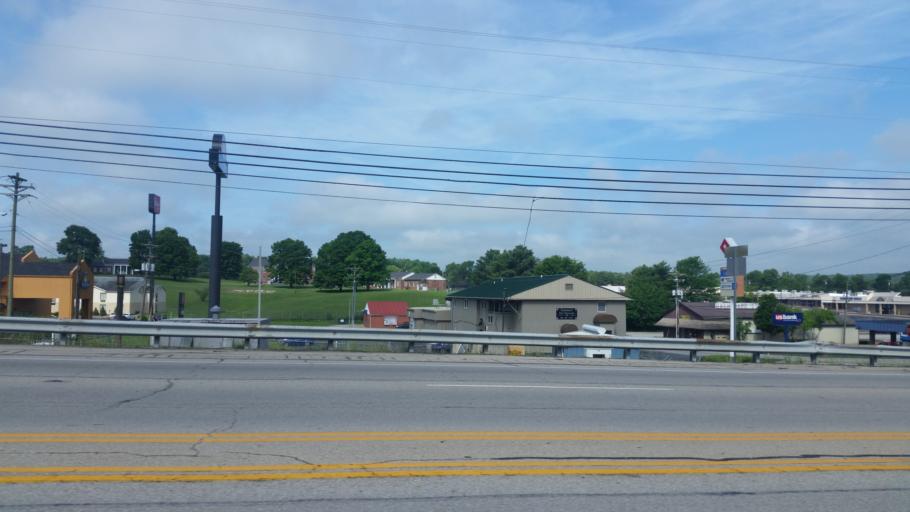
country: US
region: Kentucky
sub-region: Rowan County
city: Morehead
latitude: 38.1887
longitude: -83.4770
